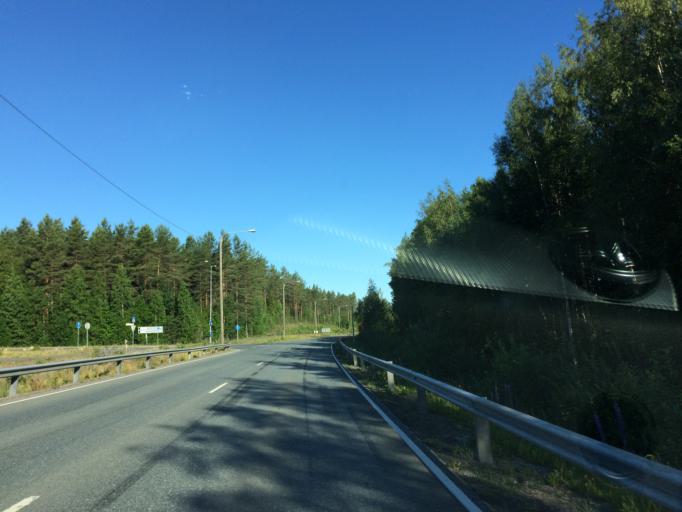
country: FI
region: Haeme
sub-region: Haemeenlinna
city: Haemeenlinna
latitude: 60.9603
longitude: 24.4577
